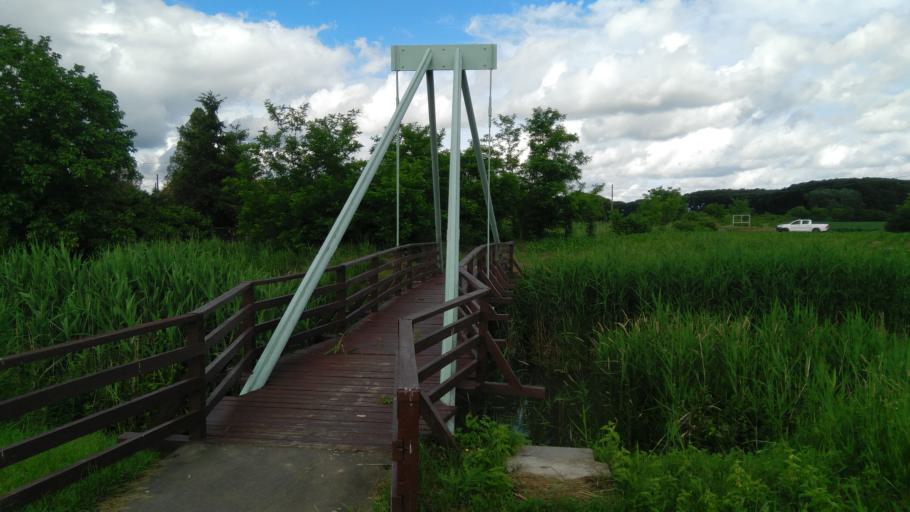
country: HU
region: Bekes
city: Bekescsaba
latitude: 46.6926
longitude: 21.1786
